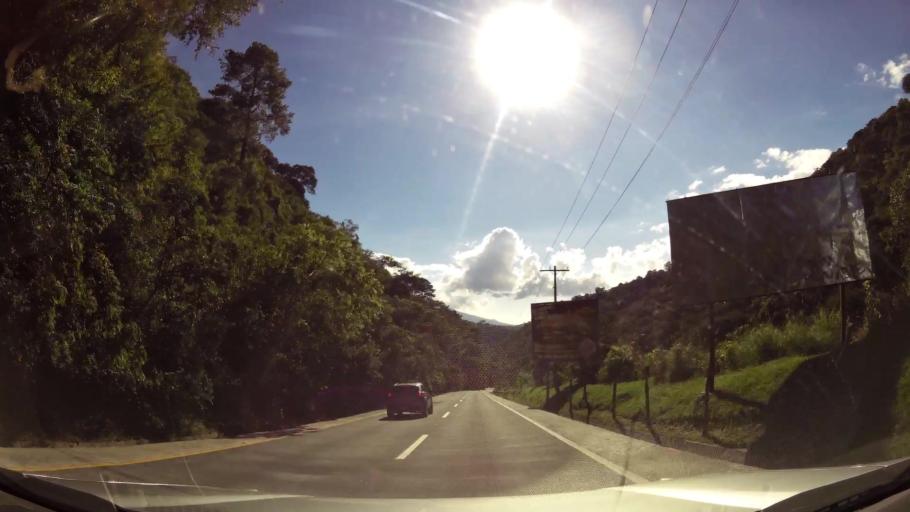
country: GT
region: Sacatepequez
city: Santa Lucia Milpas Altas
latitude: 14.5721
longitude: -90.6887
